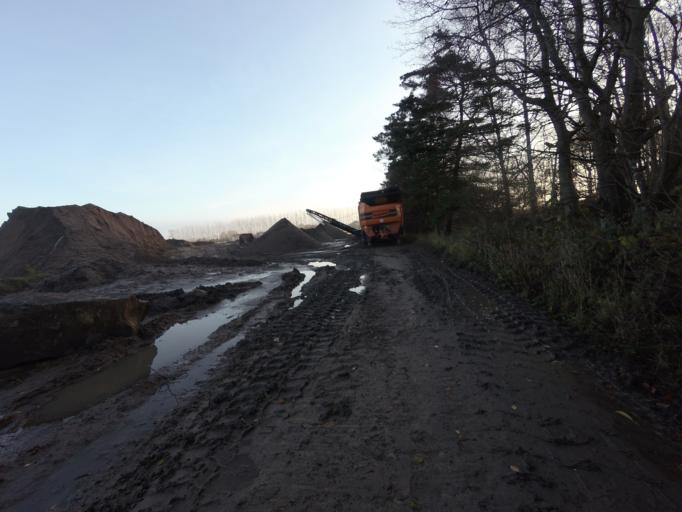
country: SE
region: Skane
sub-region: Hoganas Kommun
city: Hoganas
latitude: 56.1453
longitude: 12.5870
